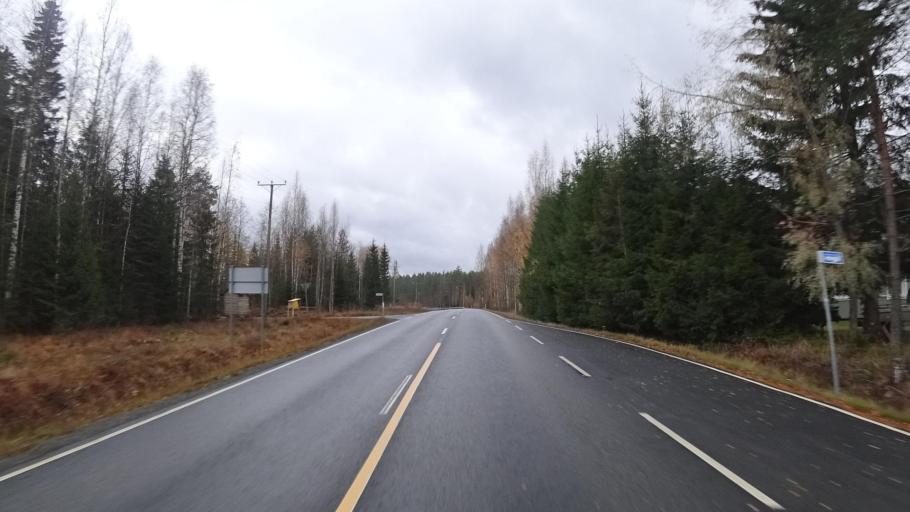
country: FI
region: Southern Savonia
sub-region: Mikkeli
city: Kangasniemi
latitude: 62.1344
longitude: 26.7759
